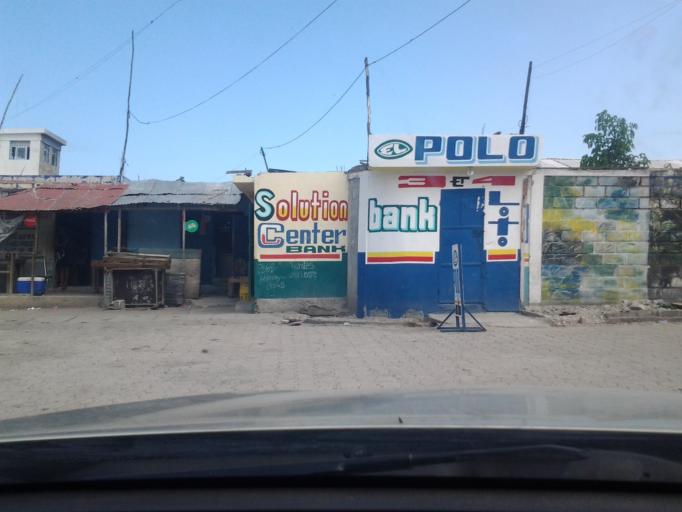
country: HT
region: Ouest
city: Tigwav
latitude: 18.4334
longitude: -72.8664
